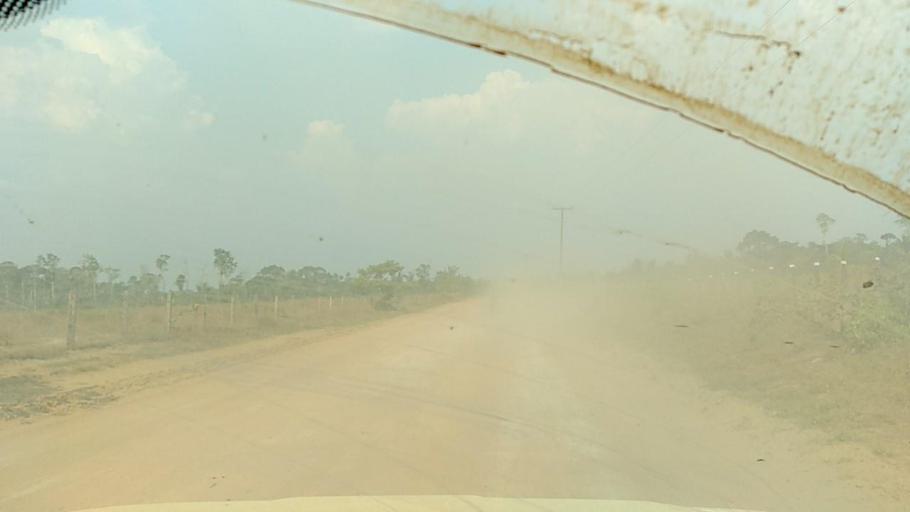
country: BR
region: Rondonia
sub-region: Porto Velho
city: Porto Velho
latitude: -8.6832
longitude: -63.1996
